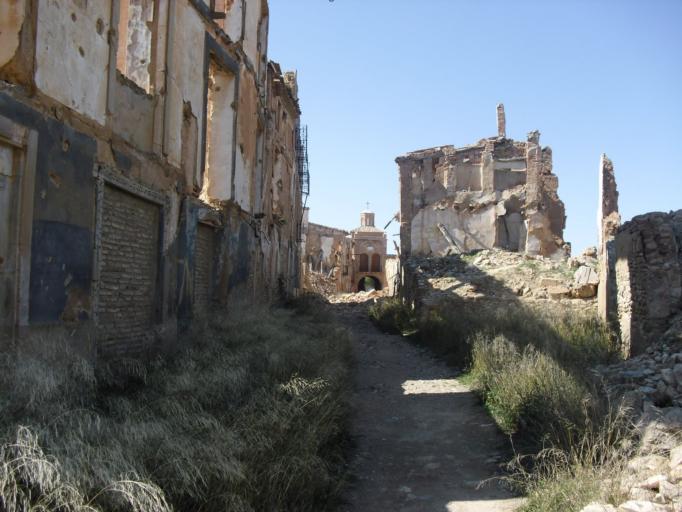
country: ES
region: Aragon
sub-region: Provincia de Zaragoza
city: Belchite
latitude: 41.3016
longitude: -0.7492
